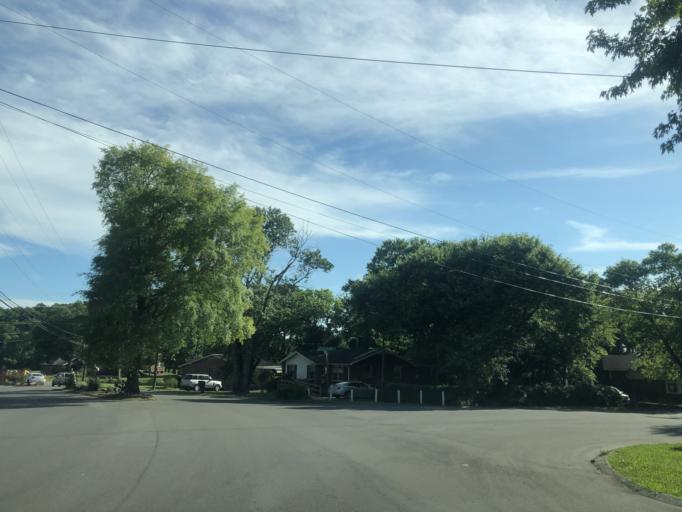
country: US
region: Tennessee
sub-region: Davidson County
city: Nashville
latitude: 36.2084
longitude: -86.8362
